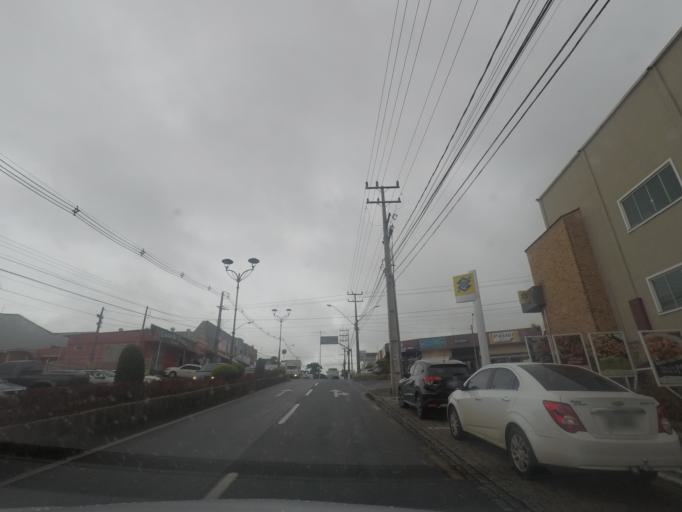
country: BR
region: Parana
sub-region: Quatro Barras
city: Quatro Barras
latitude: -25.3687
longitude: -49.0763
